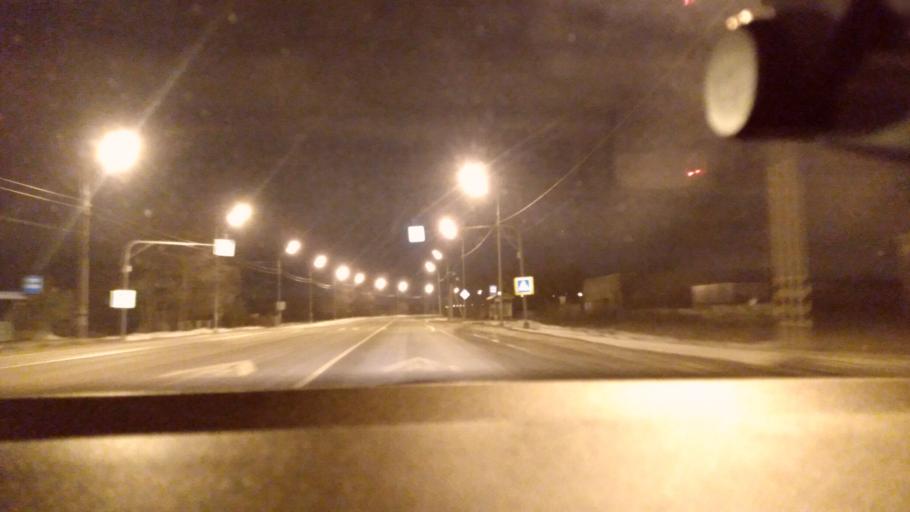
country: RU
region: Moskovskaya
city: Bronnitsy
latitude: 55.3921
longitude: 38.3269
